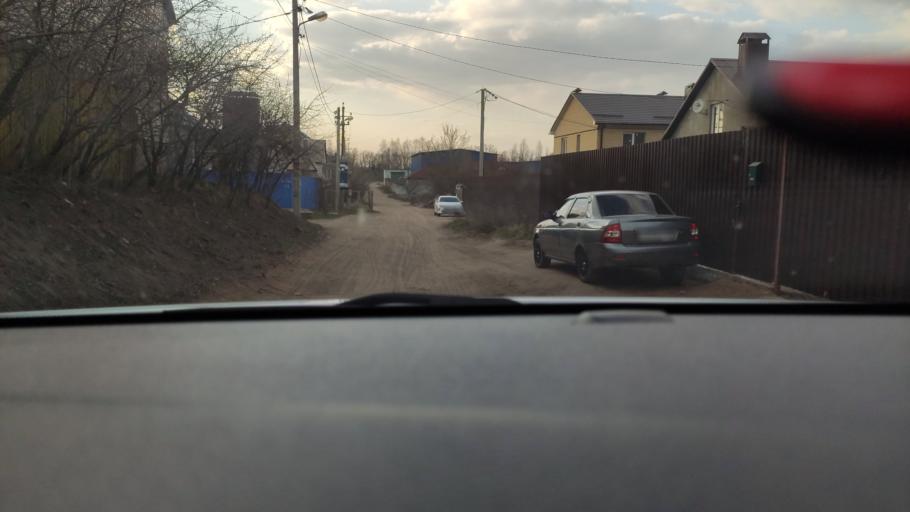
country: RU
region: Voronezj
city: Pridonskoy
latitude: 51.6373
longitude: 39.0940
